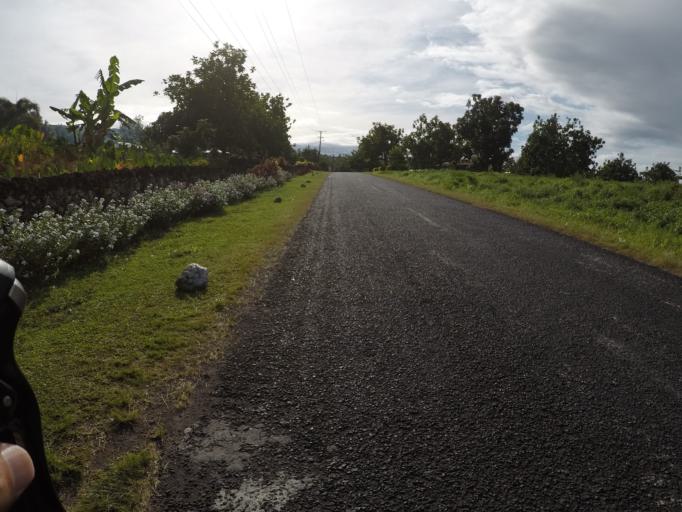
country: WS
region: Vaisigano
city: Asau
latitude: -13.6507
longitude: -172.6571
